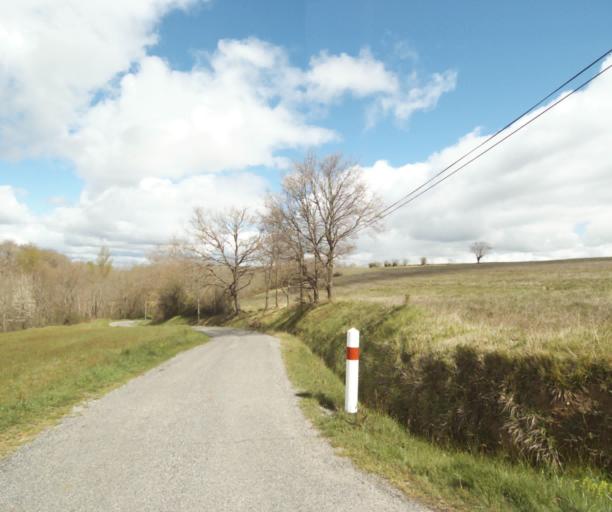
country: FR
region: Midi-Pyrenees
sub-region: Departement de l'Ariege
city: Saverdun
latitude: 43.2012
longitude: 1.5846
